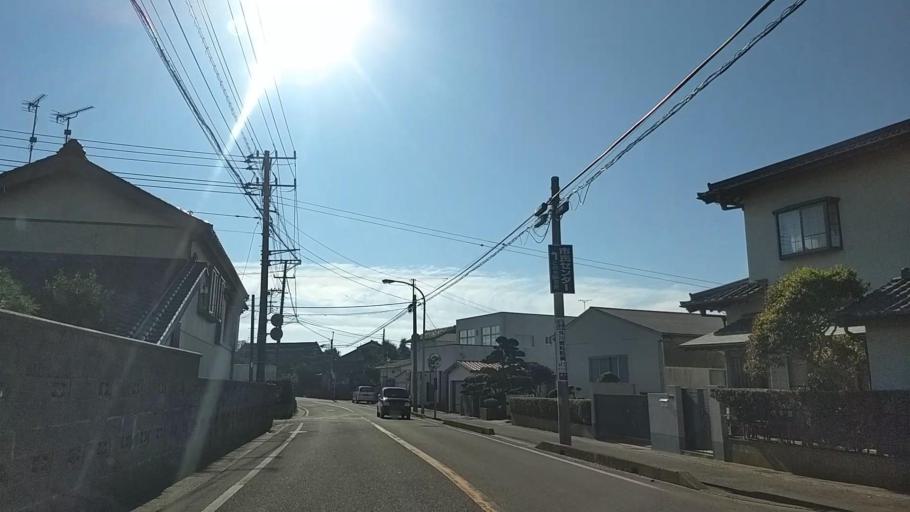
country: JP
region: Chiba
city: Hasaki
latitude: 35.7241
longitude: 140.8511
